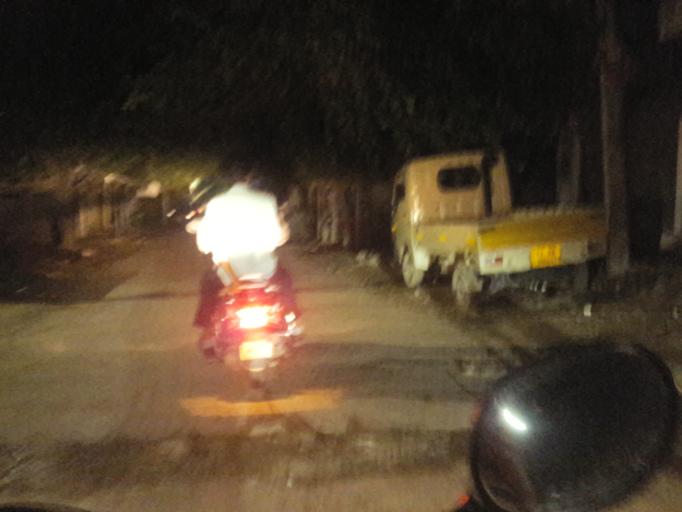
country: IN
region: Telangana
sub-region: Rangareddi
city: Kukatpalli
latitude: 17.4876
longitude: 78.3939
